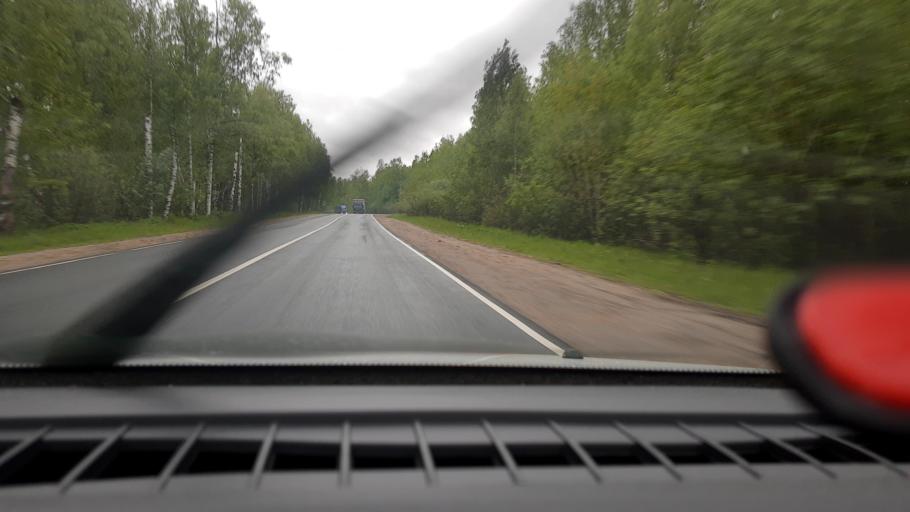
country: RU
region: Nizjnij Novgorod
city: Krasnyye Baki
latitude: 57.0716
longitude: 45.1404
